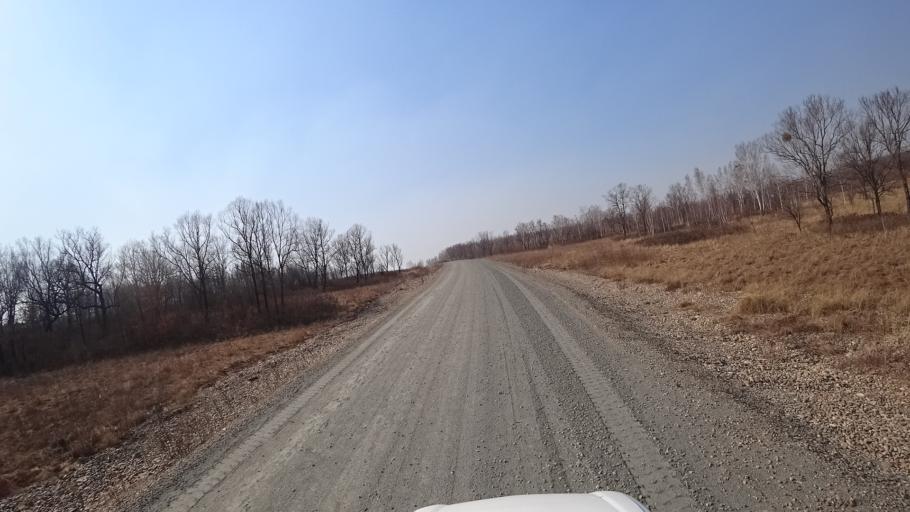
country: RU
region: Amur
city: Novobureyskiy
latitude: 49.8261
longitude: 129.9938
